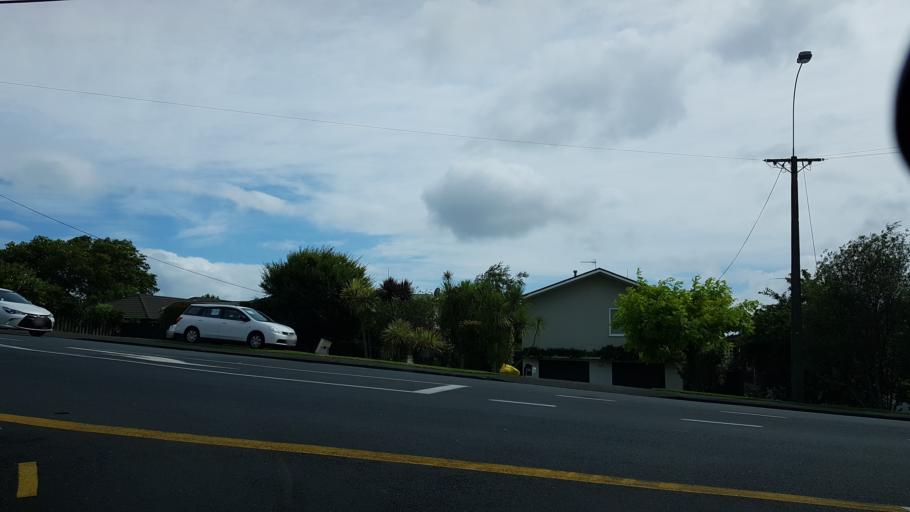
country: NZ
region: Auckland
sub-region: Auckland
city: North Shore
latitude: -36.7884
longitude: 174.7434
